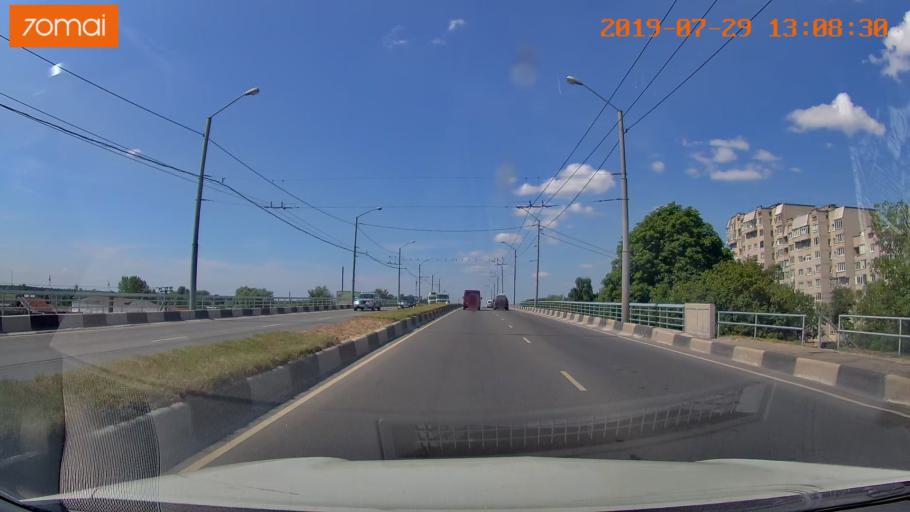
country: RU
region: Kaliningrad
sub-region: Gorod Kaliningrad
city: Kaliningrad
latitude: 54.7118
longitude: 20.4309
